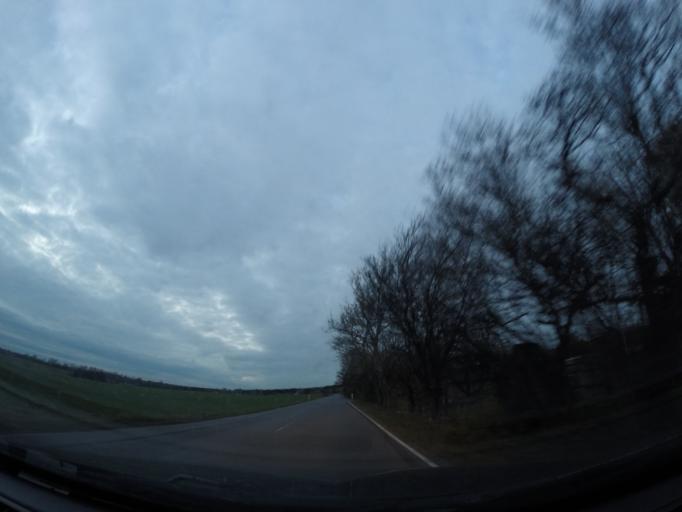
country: DK
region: Capital Region
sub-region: Hoje-Taastrup Kommune
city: Taastrup
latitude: 55.6812
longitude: 12.3076
